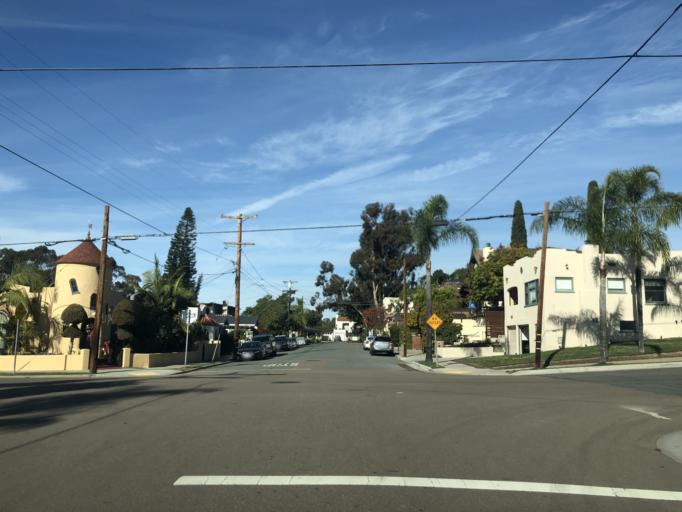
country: US
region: California
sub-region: San Diego County
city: San Diego
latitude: 32.7263
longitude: -117.1329
